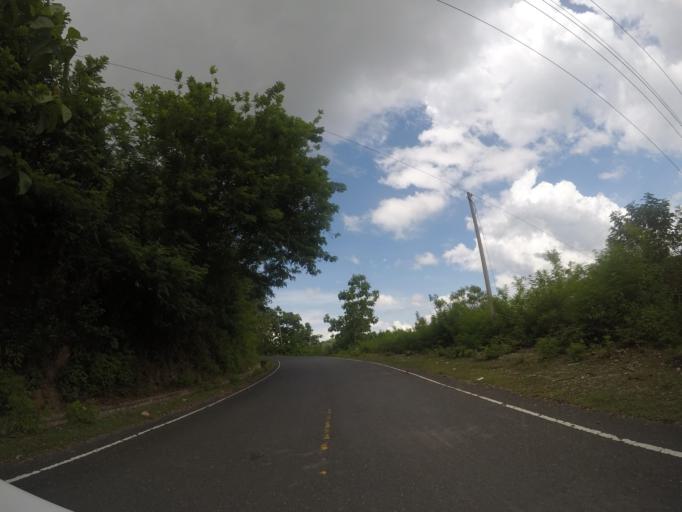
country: TL
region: Bobonaro
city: Maliana
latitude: -8.9537
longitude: 125.0843
